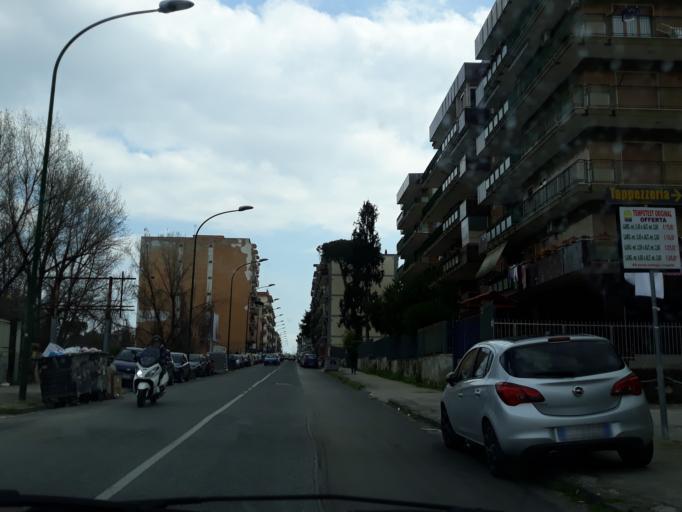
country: IT
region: Campania
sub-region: Provincia di Napoli
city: Mugnano di Napoli
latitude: 40.8844
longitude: 14.2298
